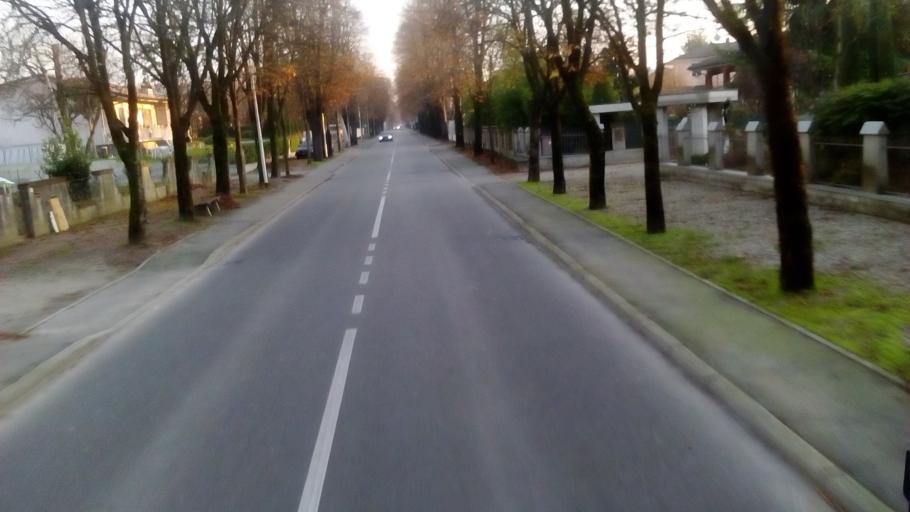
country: IT
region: Lombardy
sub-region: Provincia di Cremona
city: Castelleone
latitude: 45.3032
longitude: 9.7555
